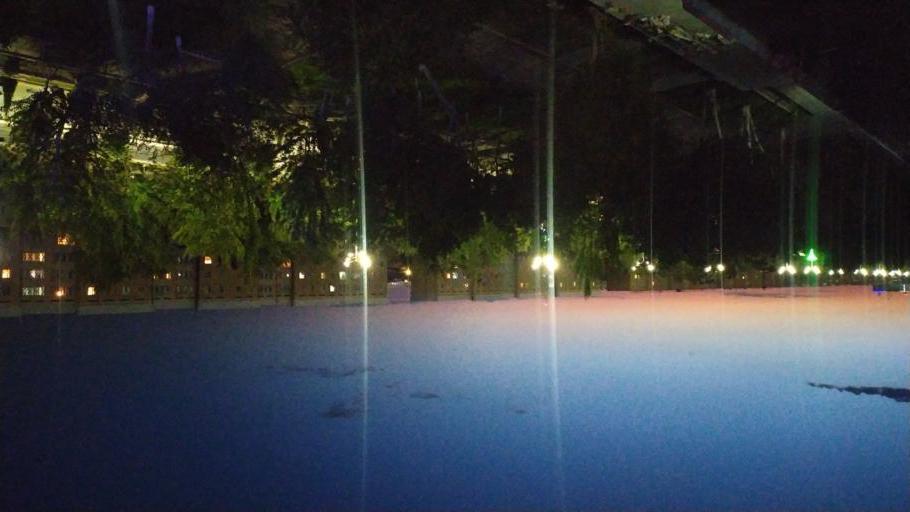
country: UZ
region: Karakalpakstan
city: Nukus
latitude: 42.4485
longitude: 59.6153
